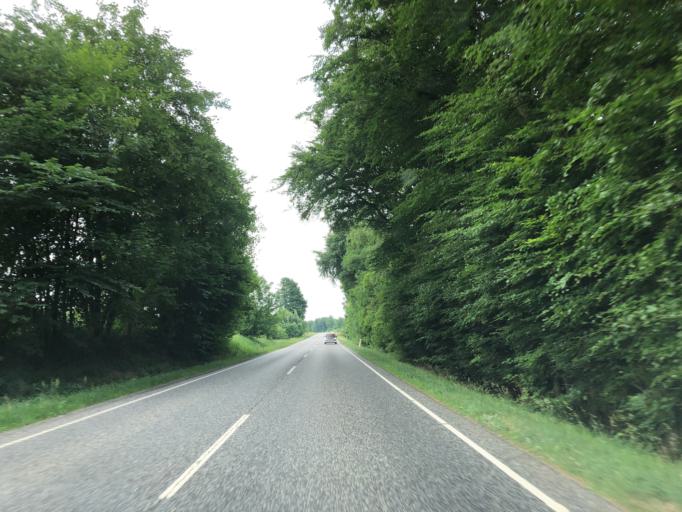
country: DK
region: South Denmark
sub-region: Vejle Kommune
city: Give
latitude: 55.7765
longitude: 9.2814
